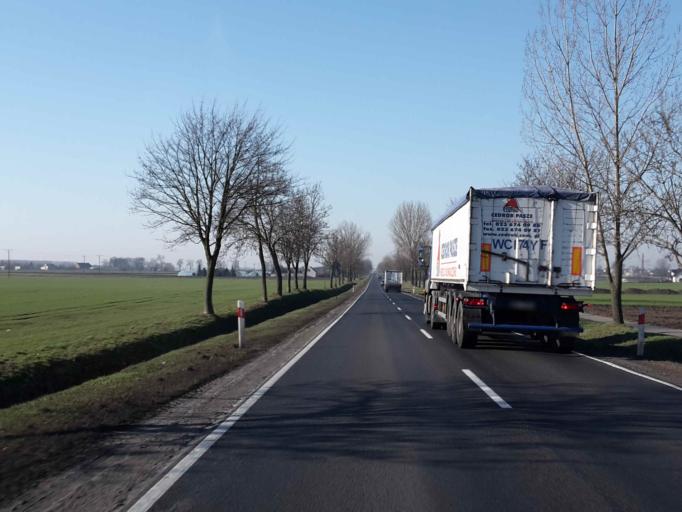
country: PL
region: Kujawsko-Pomorskie
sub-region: Powiat inowroclawski
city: Wierzchoslawice
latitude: 52.8760
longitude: 18.3778
